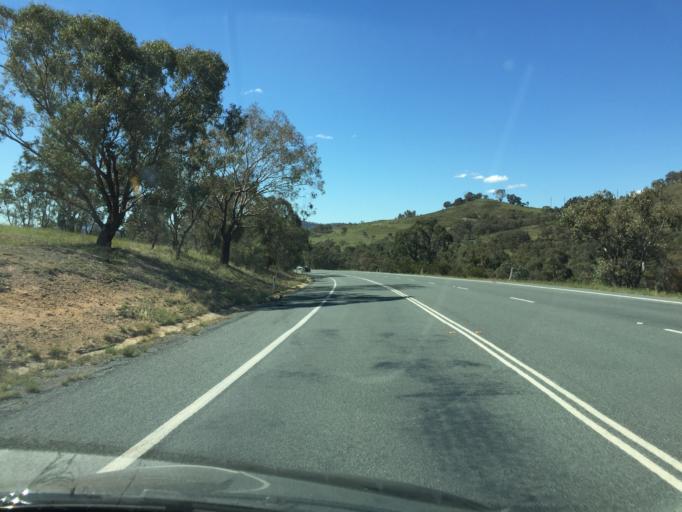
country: AU
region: Australian Capital Territory
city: Macarthur
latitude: -35.4457
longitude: 149.1307
